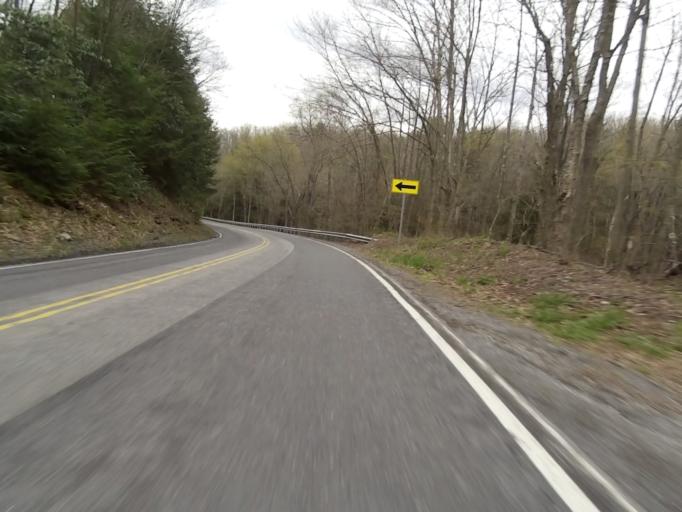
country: US
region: Pennsylvania
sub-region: Clearfield County
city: Troy
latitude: 40.9089
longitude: -78.0943
